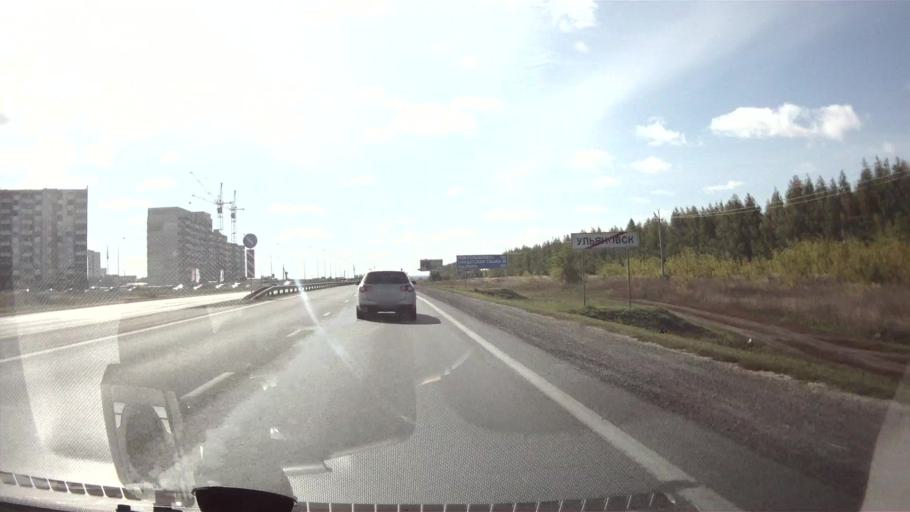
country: RU
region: Ulyanovsk
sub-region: Ulyanovskiy Rayon
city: Ulyanovsk
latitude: 54.2845
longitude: 48.2572
